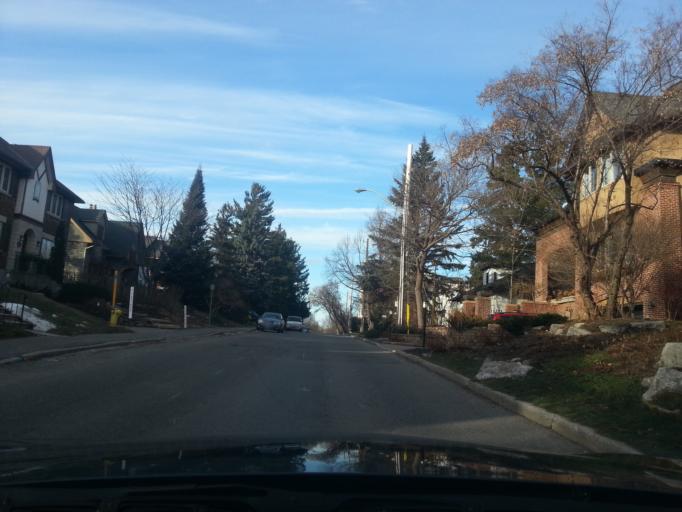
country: CA
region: Ontario
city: Ottawa
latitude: 45.4226
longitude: -75.6693
